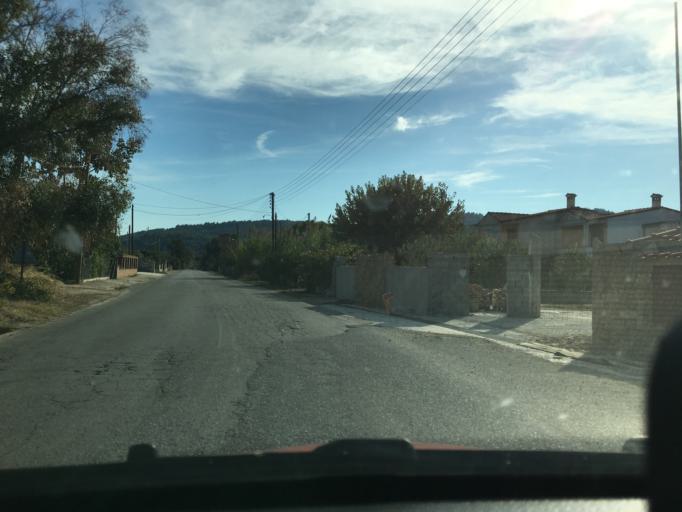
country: GR
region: Central Macedonia
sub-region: Nomos Chalkidikis
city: Agios Nikolaos
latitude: 40.2978
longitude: 23.6945
